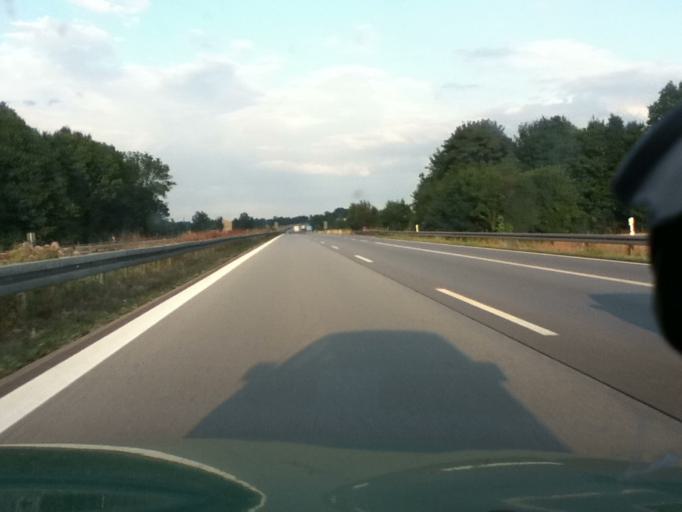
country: DE
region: Saxony
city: Goda
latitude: 51.1984
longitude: 14.3337
